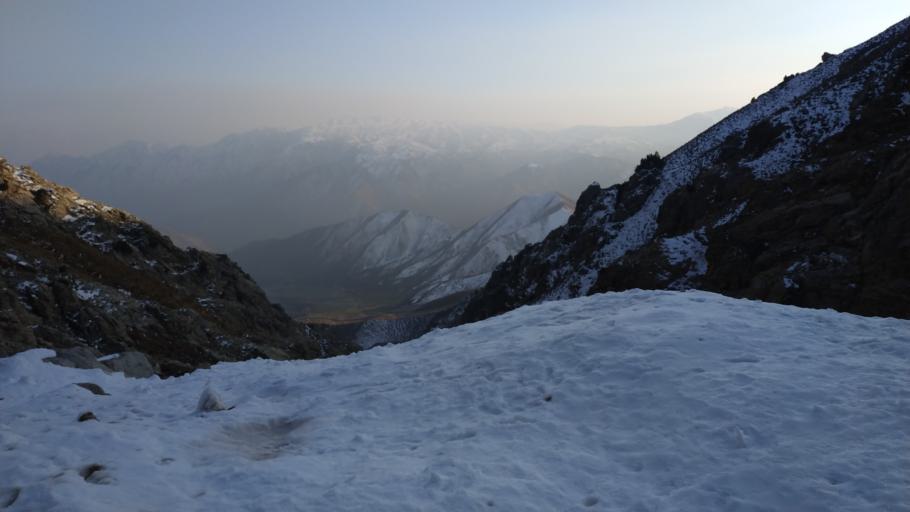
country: TJ
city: Varzob
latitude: 38.9053
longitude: 68.7456
